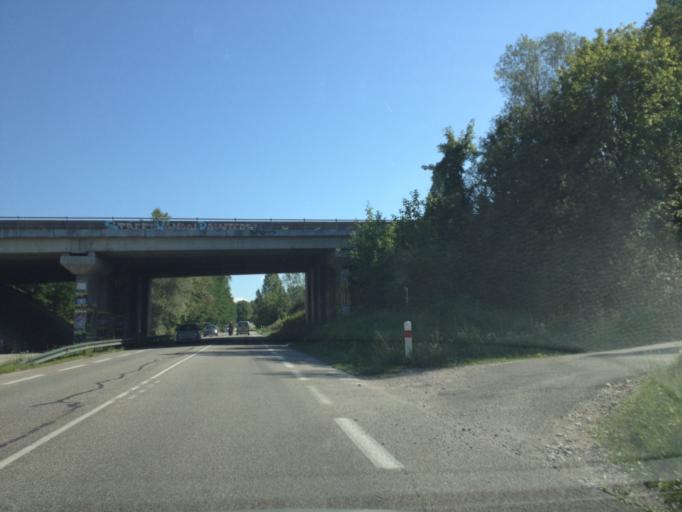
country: FR
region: Rhone-Alpes
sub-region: Departement de la Savoie
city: Voglans
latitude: 45.6331
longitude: 5.9133
